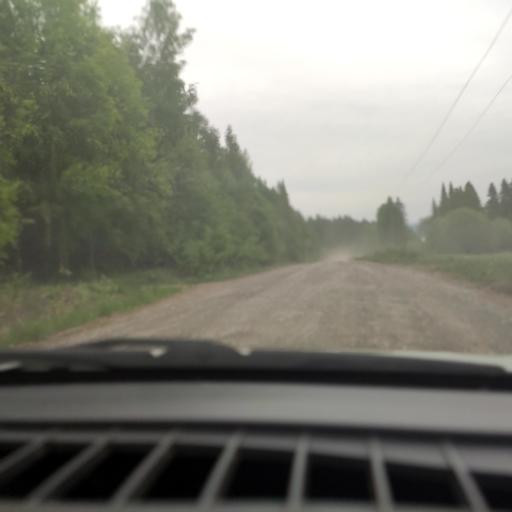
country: RU
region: Perm
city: Novyye Lyady
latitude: 57.9162
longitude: 56.6590
